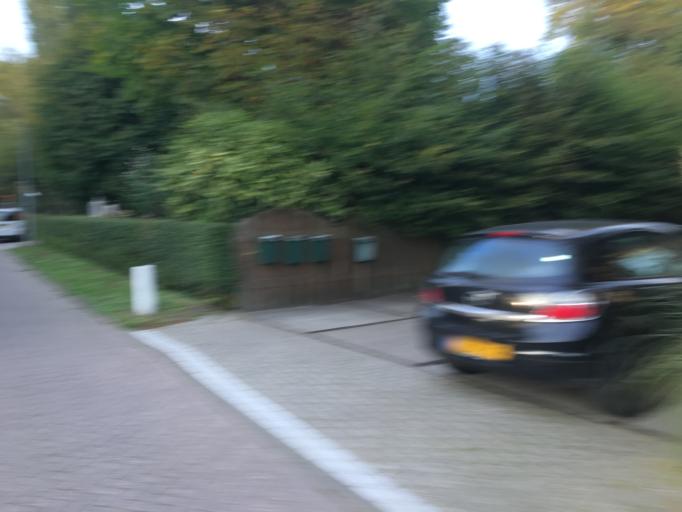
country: NL
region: North Holland
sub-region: Gemeente Zaanstad
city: Zaanstad
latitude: 52.4386
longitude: 4.7790
